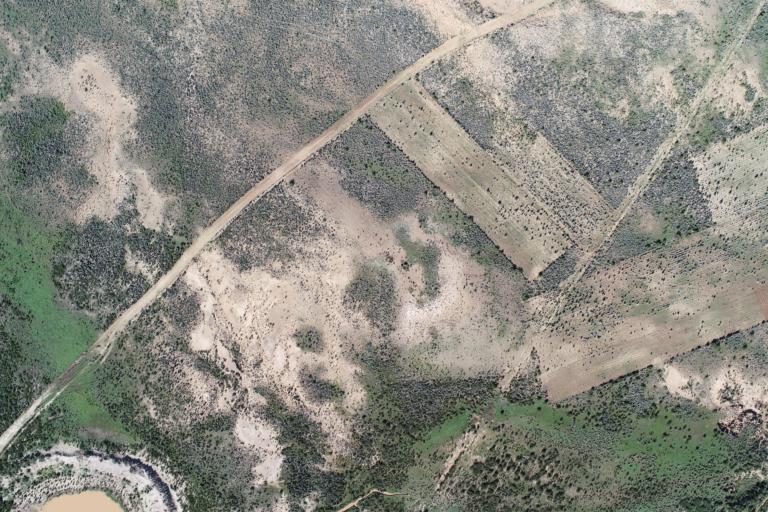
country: BO
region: La Paz
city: Curahuara de Carangas
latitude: -17.3024
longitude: -68.5156
